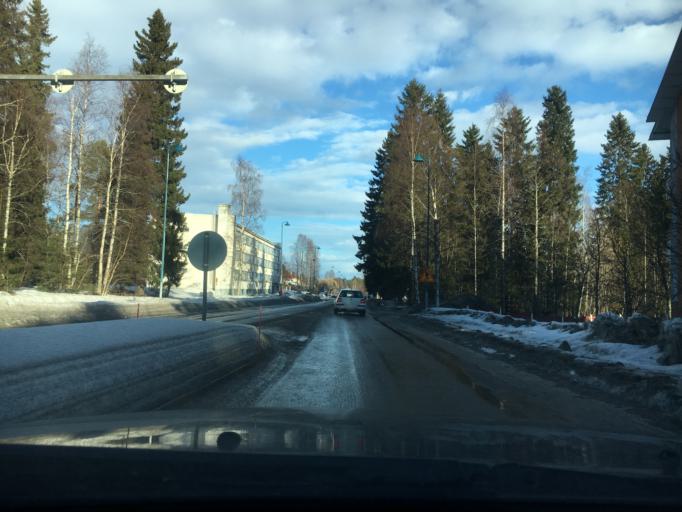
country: FI
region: Kainuu
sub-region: Kajaani
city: Kajaani
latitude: 64.2298
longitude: 27.7536
